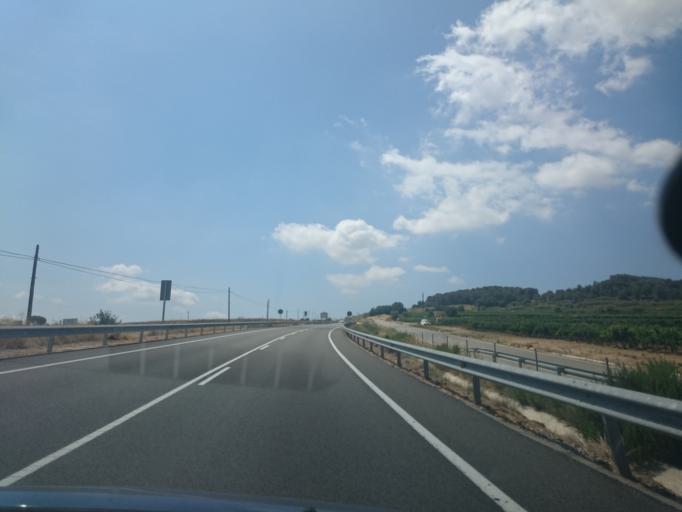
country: ES
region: Catalonia
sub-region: Provincia de Barcelona
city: La Granada
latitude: 41.3940
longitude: 1.7091
